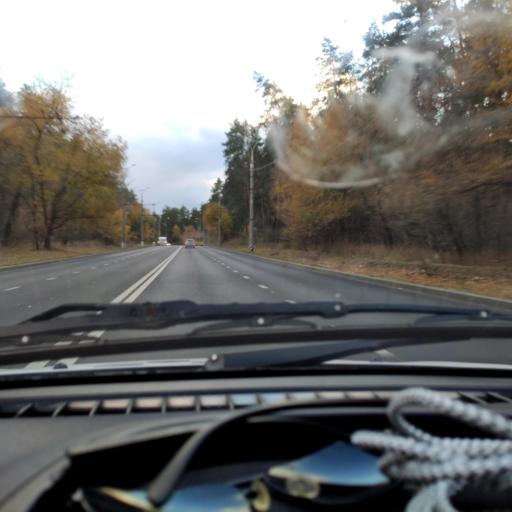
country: RU
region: Samara
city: Zhigulevsk
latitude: 53.4906
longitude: 49.4627
